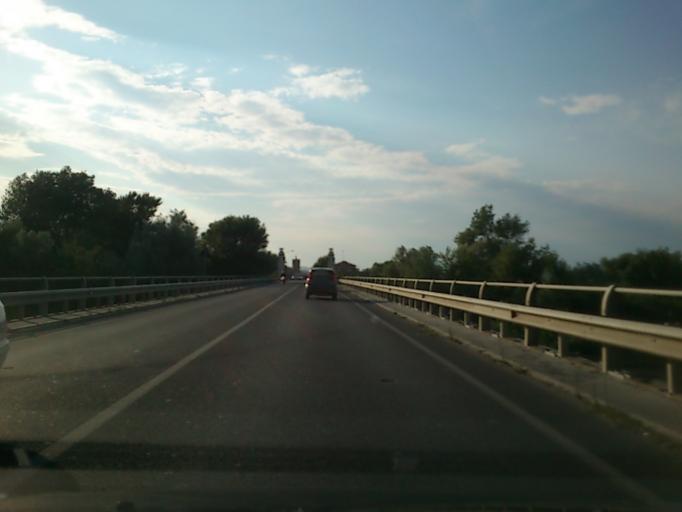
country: IT
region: The Marches
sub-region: Provincia di Pesaro e Urbino
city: Fano
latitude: 43.8269
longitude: 13.0529
